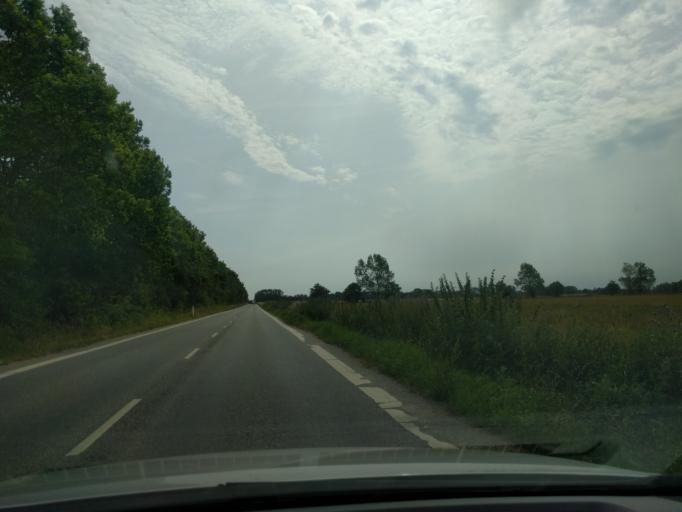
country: DK
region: South Denmark
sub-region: Nordfyns Kommune
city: Otterup
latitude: 55.5569
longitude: 10.4636
